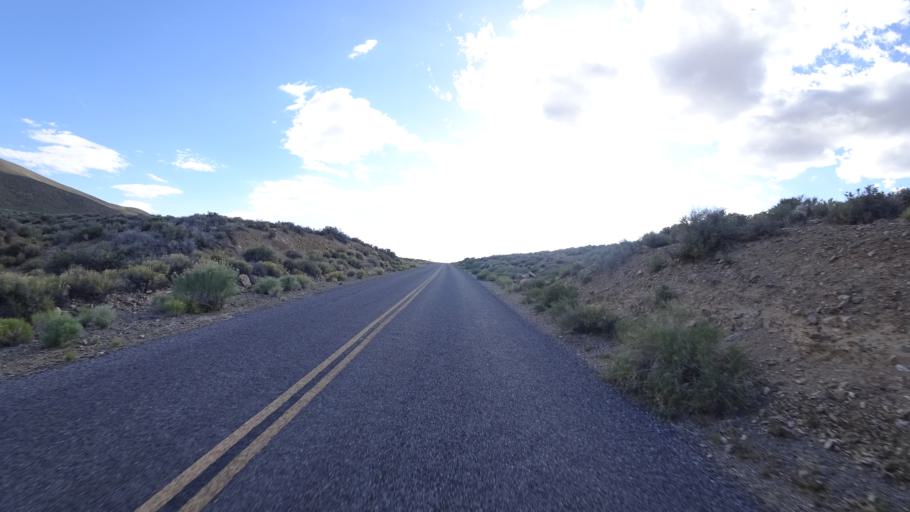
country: US
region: California
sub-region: San Bernardino County
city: Searles Valley
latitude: 36.3354
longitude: -117.1390
